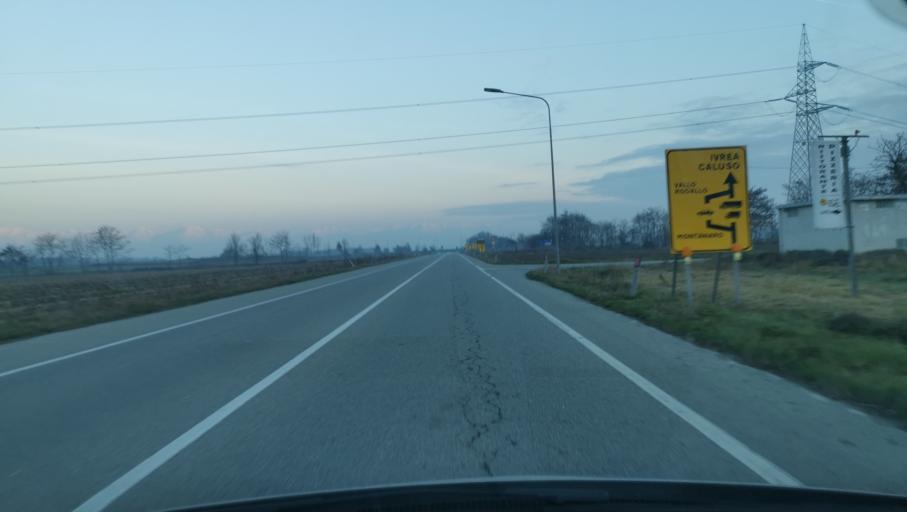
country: IT
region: Piedmont
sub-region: Provincia di Torino
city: Chivasso
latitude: 45.2246
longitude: 7.8908
